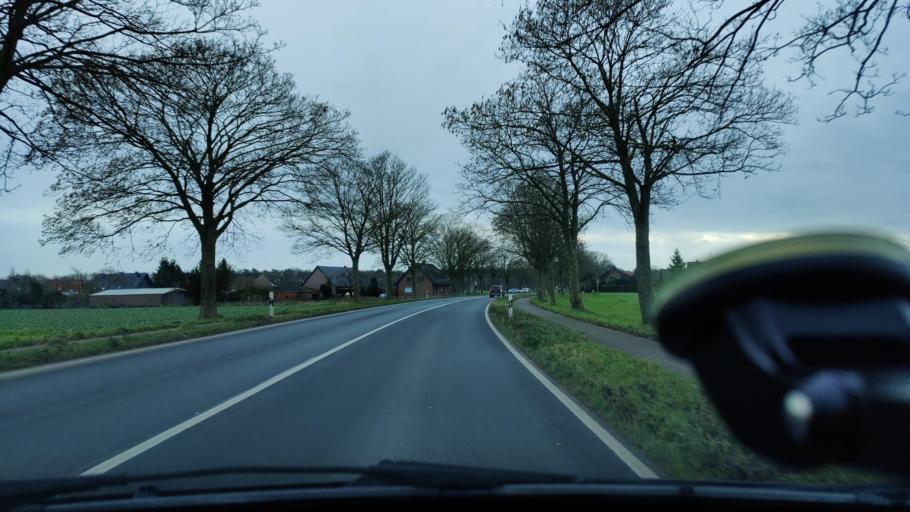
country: DE
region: North Rhine-Westphalia
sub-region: Regierungsbezirk Dusseldorf
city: Alpen
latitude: 51.5710
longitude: 6.4931
